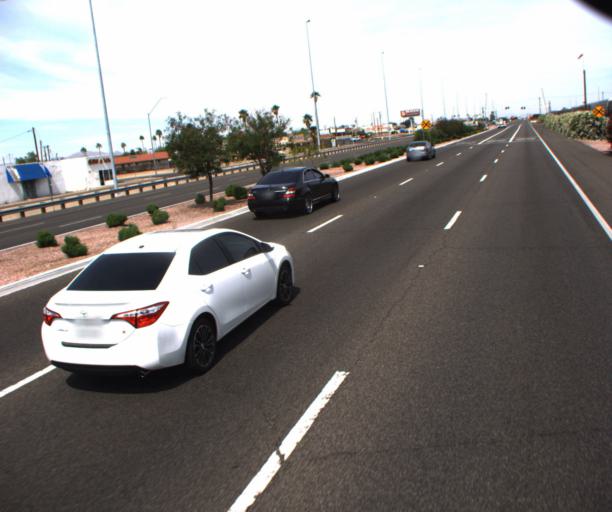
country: US
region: Arizona
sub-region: Maricopa County
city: El Mirage
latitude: 33.6164
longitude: -112.3215
